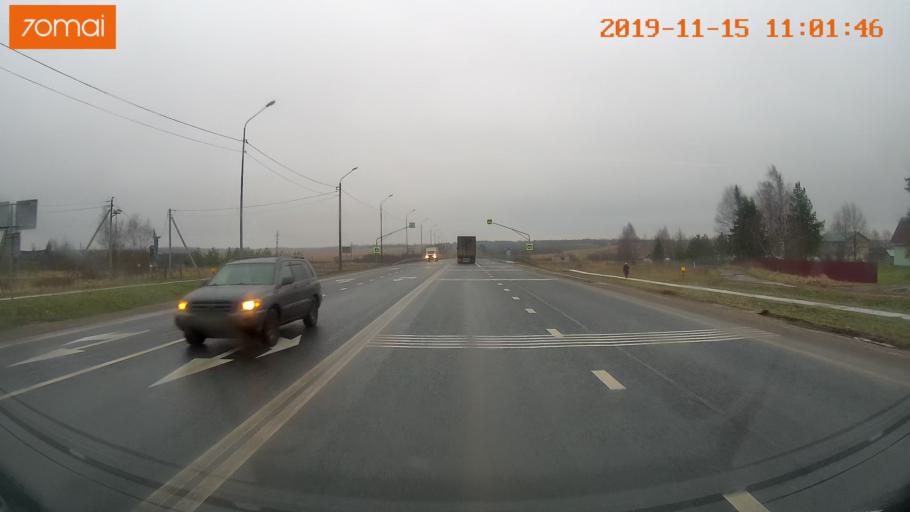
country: RU
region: Vologda
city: Chebsara
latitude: 59.1316
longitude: 38.9270
